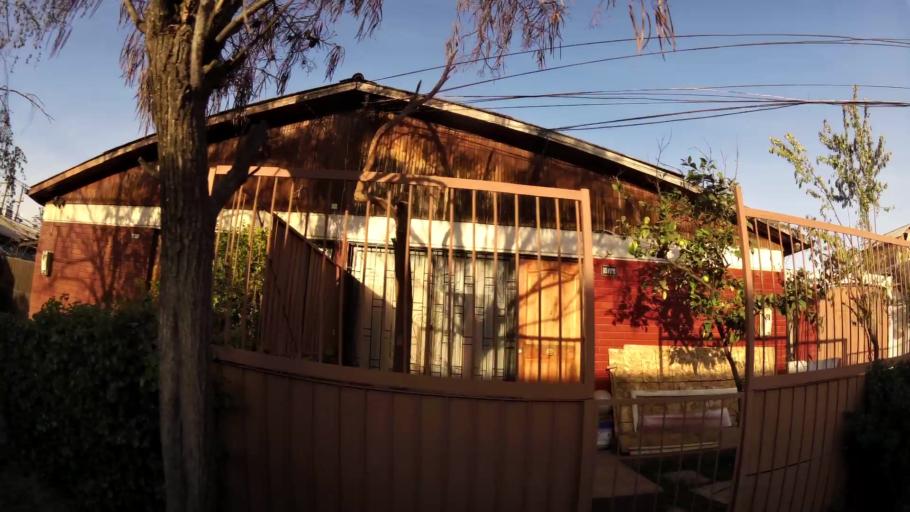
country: CL
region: Santiago Metropolitan
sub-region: Provincia de Cordillera
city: Puente Alto
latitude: -33.5565
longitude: -70.5822
